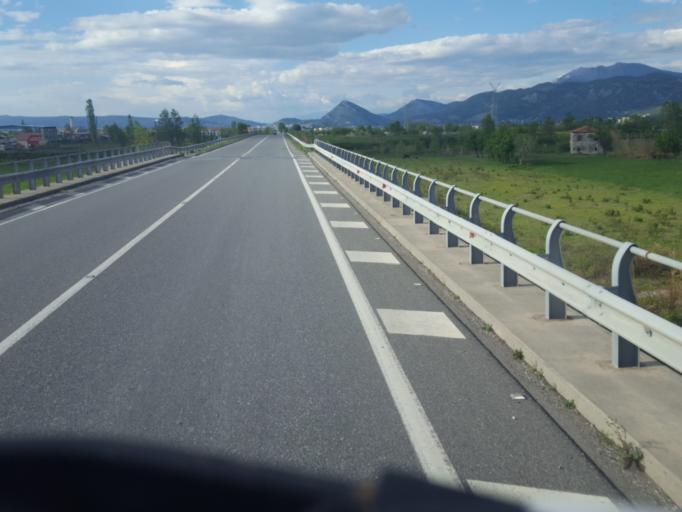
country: AL
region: Lezhe
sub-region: Rrethi i Lezhes
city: Shenkoll
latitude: 41.6862
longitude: 19.6716
